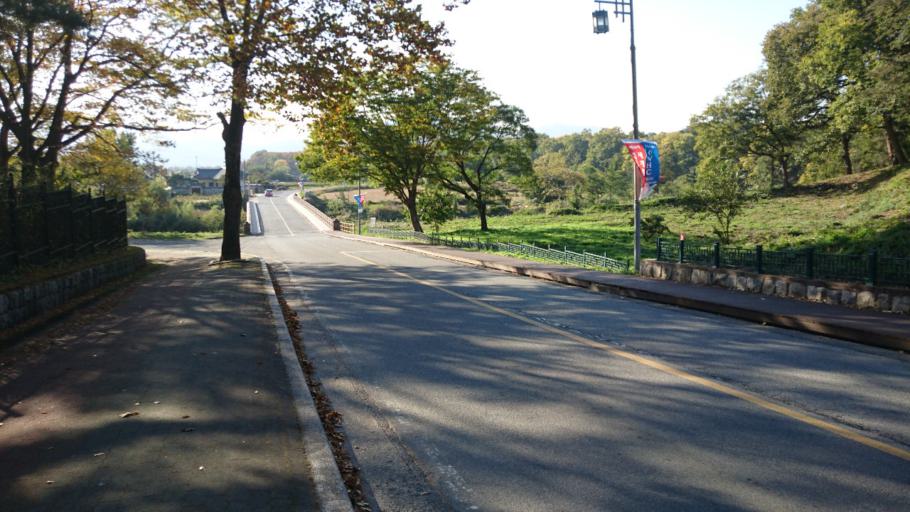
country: KR
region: Gyeongsangbuk-do
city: Kyonju
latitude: 35.8302
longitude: 129.2272
